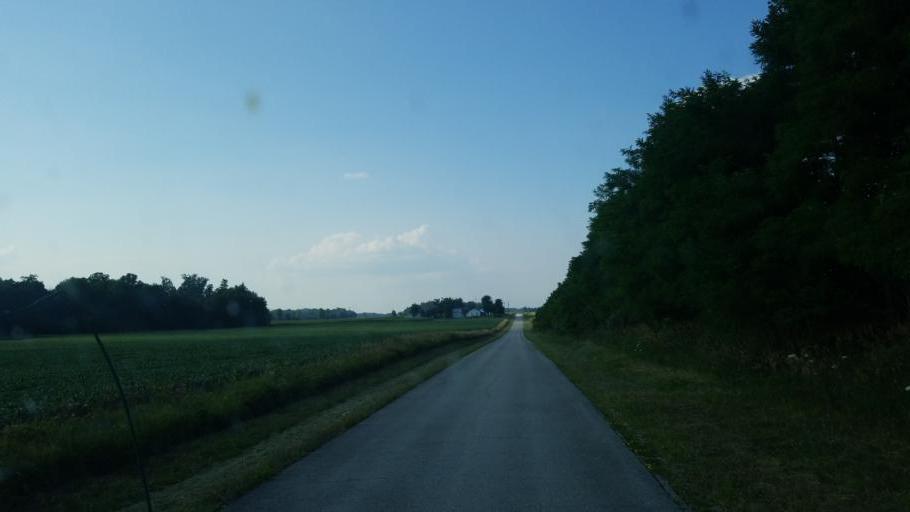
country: US
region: Ohio
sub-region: Crawford County
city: Bucyrus
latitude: 40.8594
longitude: -83.0740
